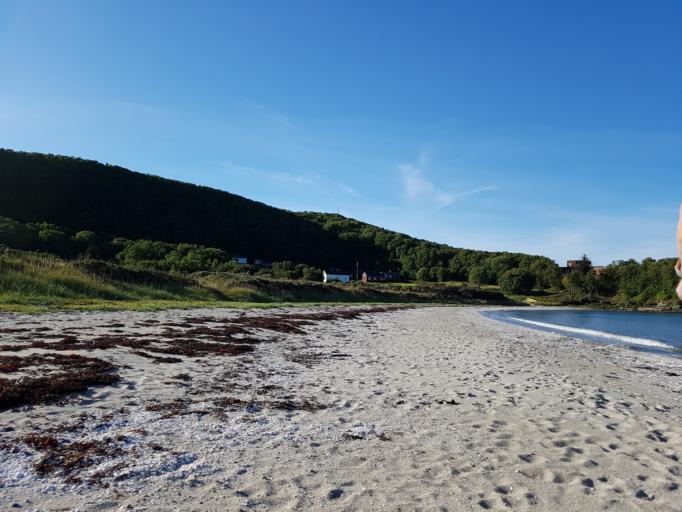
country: NO
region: Sor-Trondelag
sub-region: Afjord
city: A i Afjord
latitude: 64.0521
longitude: 9.9491
